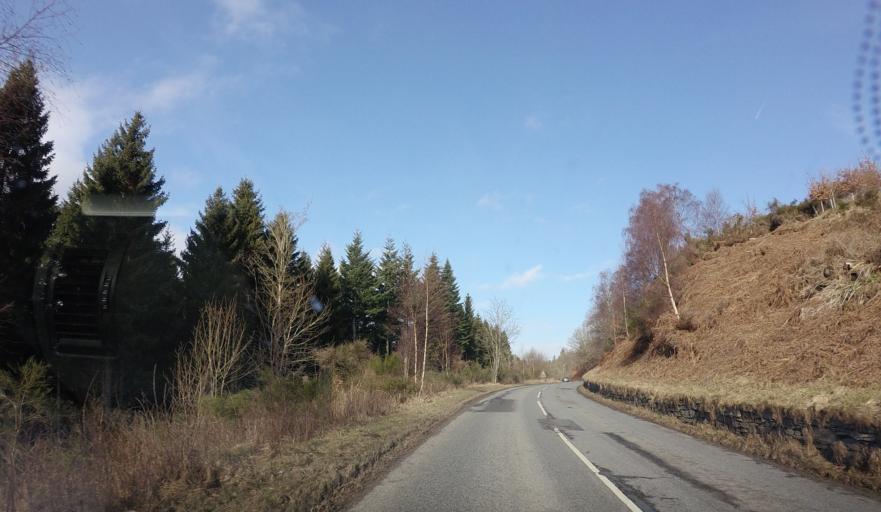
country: GB
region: Scotland
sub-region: Perth and Kinross
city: Pitlochry
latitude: 56.6002
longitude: -3.6247
